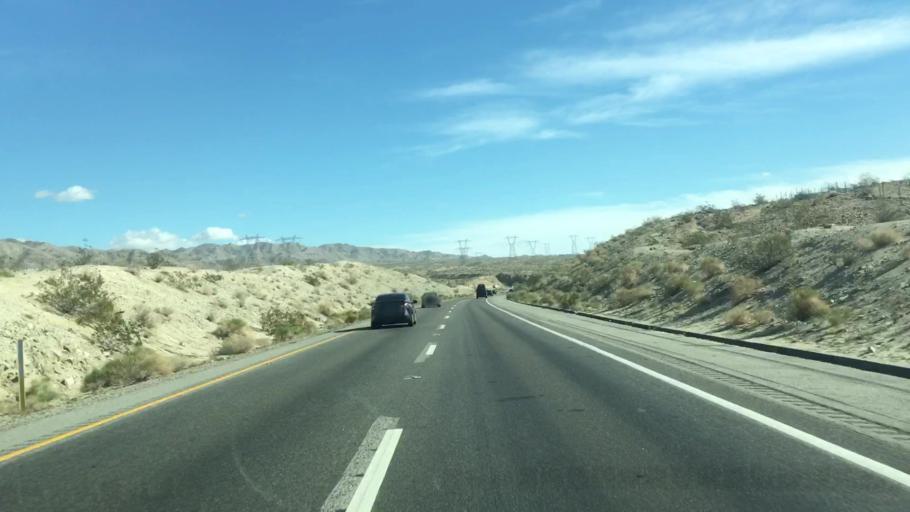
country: US
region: California
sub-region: Riverside County
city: Thermal
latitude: 33.6996
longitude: -116.0694
